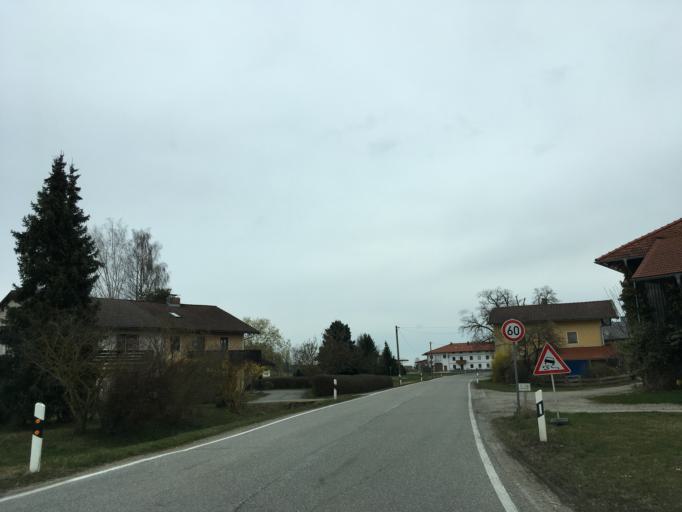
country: DE
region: Bavaria
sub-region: Upper Bavaria
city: Schnaitsee
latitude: 48.0740
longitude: 12.3916
